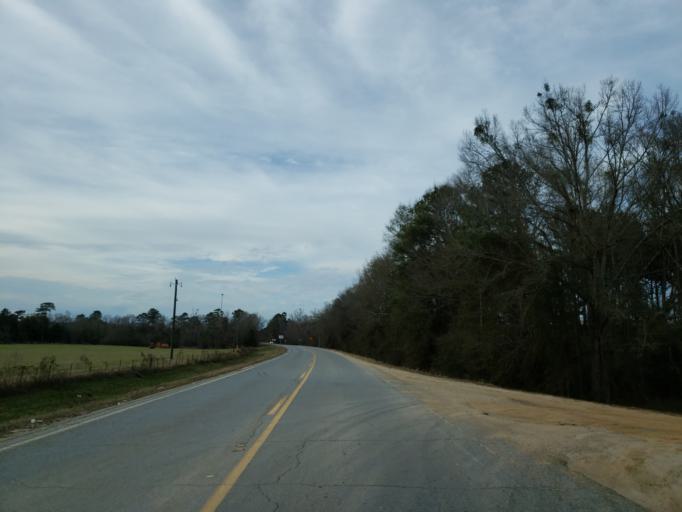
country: US
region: Mississippi
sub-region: Clarke County
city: Quitman
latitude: 31.8713
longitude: -88.7037
